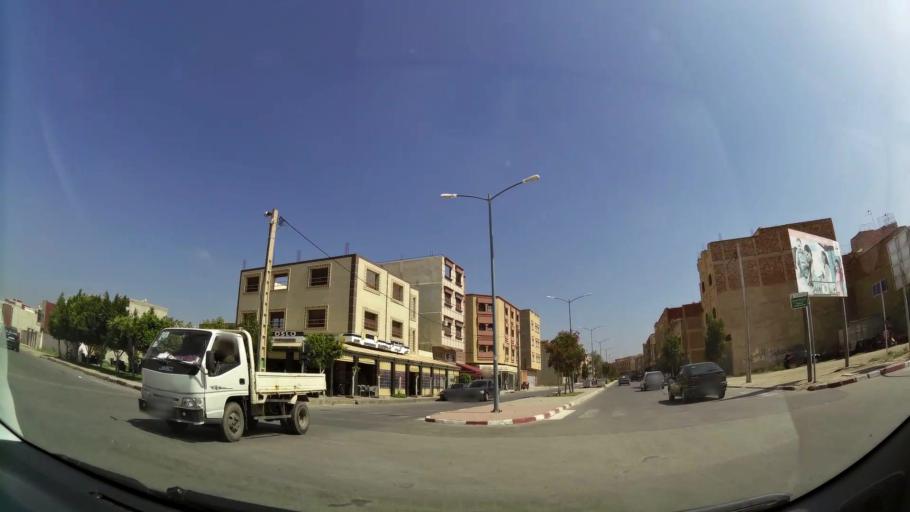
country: MA
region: Oriental
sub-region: Oujda-Angad
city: Oujda
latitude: 34.6858
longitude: -1.8745
